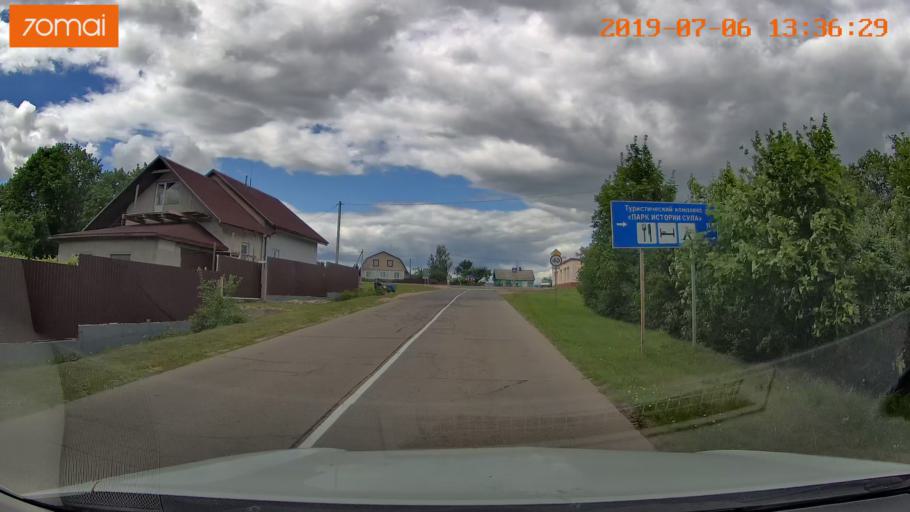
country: BY
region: Minsk
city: Enyerhyetykaw
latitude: 53.6899
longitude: 26.8657
